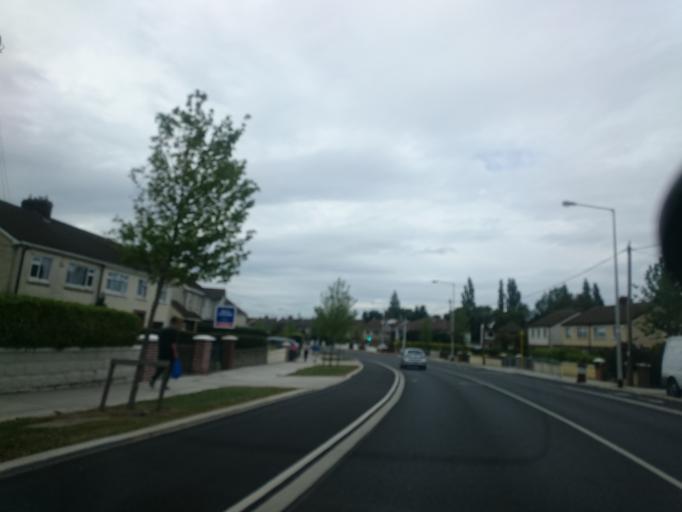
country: IE
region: Leinster
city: Dundrum
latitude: 53.2981
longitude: -6.2598
